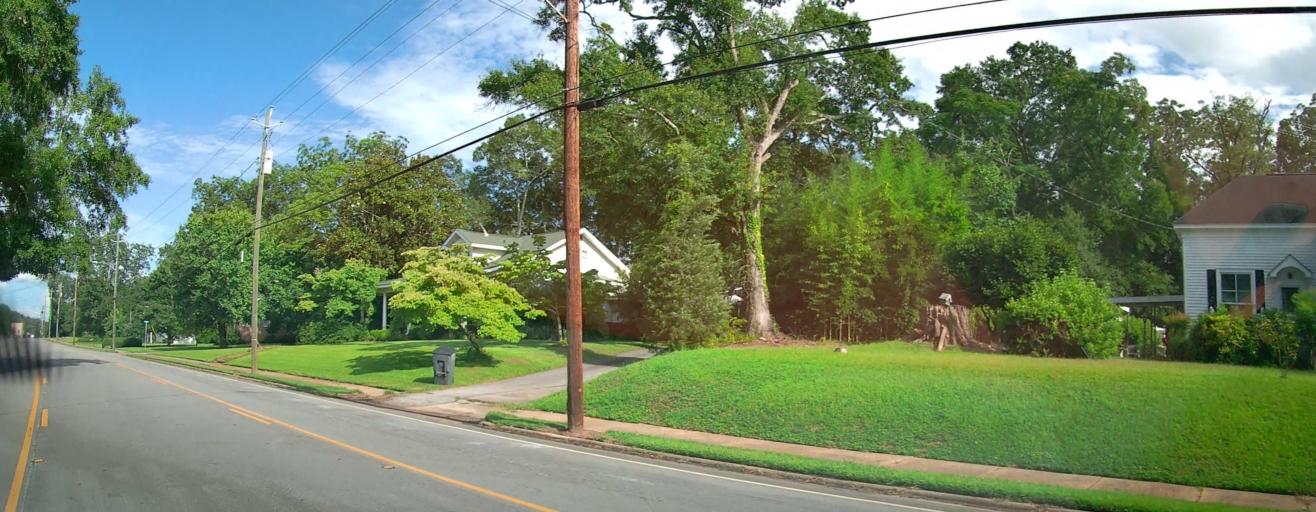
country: US
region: Georgia
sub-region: Meriwether County
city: Manchester
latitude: 32.9832
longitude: -84.5880
